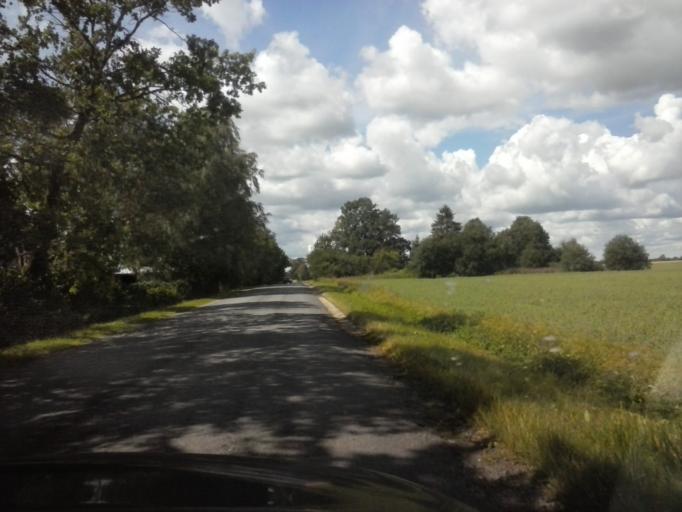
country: EE
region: Laeaene-Virumaa
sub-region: Vaeike-Maarja vald
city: Vaike-Maarja
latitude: 59.0572
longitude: 26.3410
